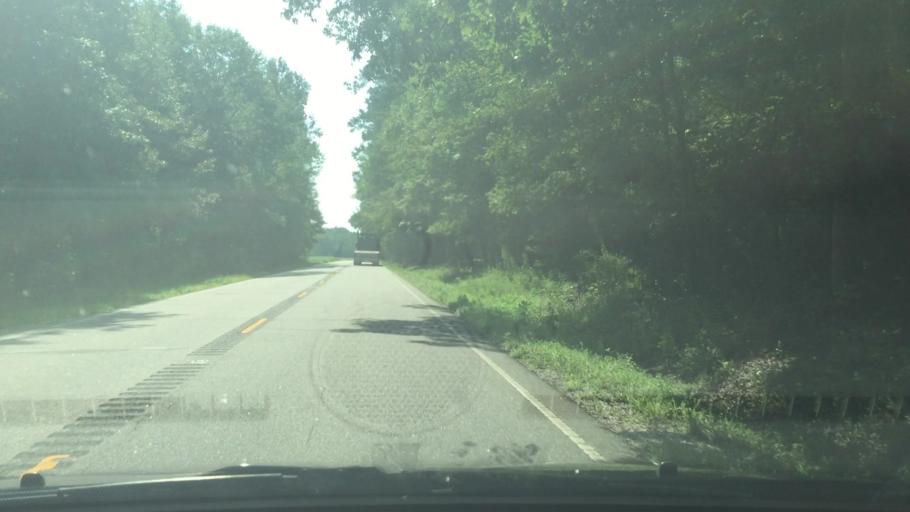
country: US
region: Virginia
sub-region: Sussex County
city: Sussex
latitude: 36.9871
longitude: -77.2495
